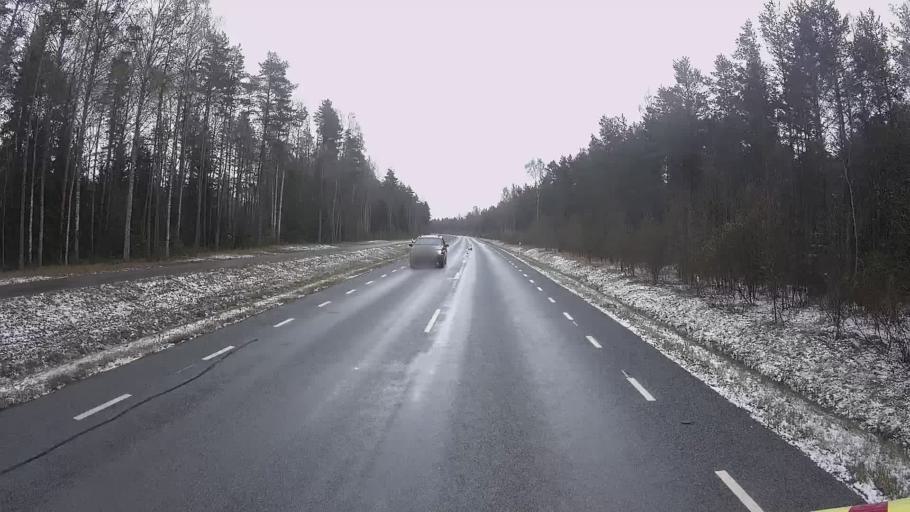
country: EE
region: Hiiumaa
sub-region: Kaerdla linn
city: Kardla
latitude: 59.0076
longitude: 22.6830
